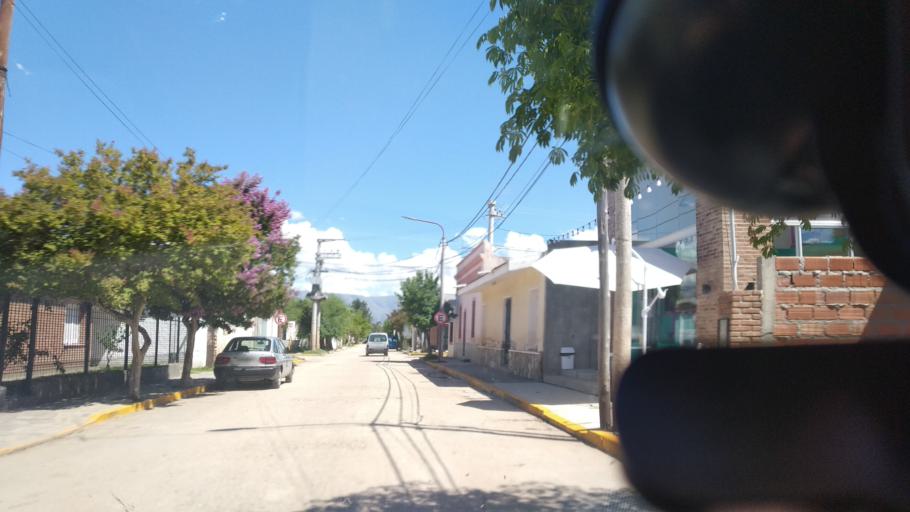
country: AR
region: Cordoba
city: Villa Cura Brochero
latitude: -31.7075
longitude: -65.0188
